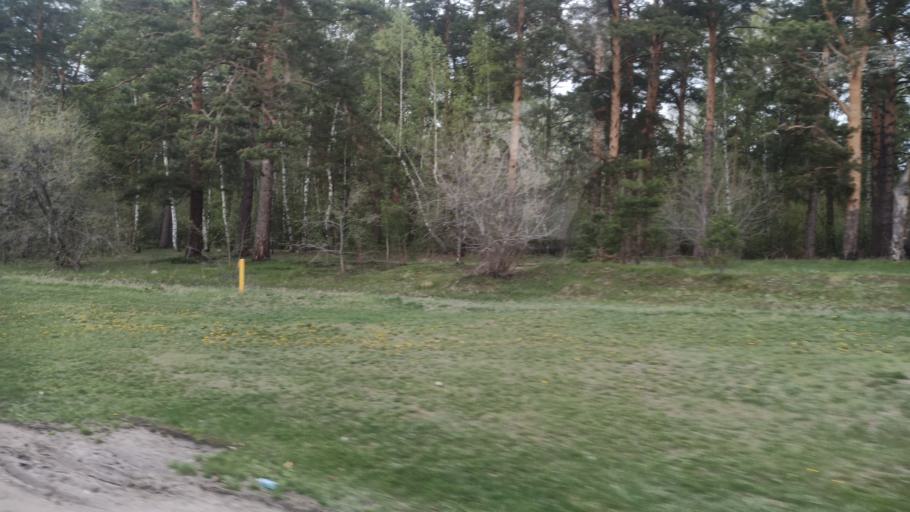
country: RU
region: Altai Krai
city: Yuzhnyy
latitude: 53.2606
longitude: 83.7001
